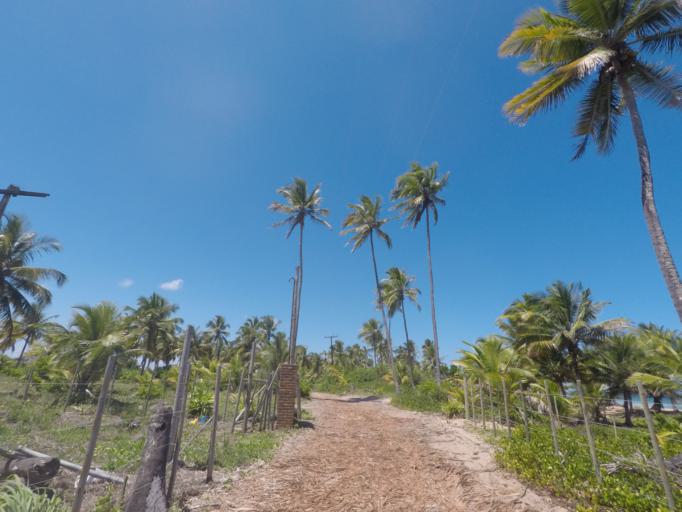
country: BR
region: Bahia
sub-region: Marau
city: Marau
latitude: -14.0022
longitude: -38.9446
